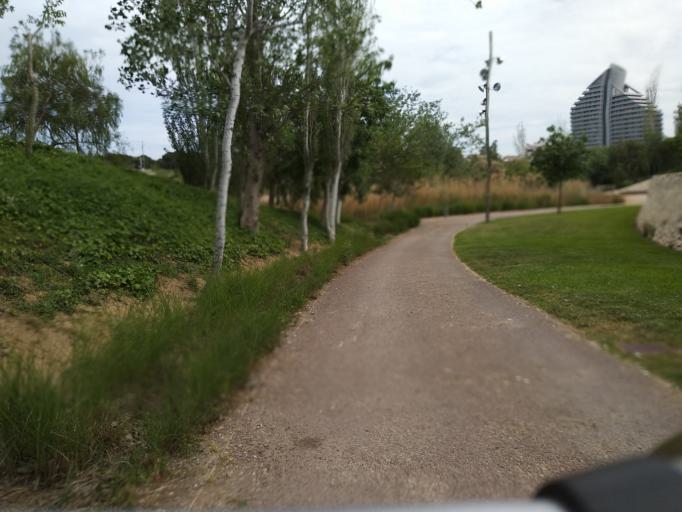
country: ES
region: Valencia
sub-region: Provincia de Valencia
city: Mislata
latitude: 39.4767
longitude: -0.4093
